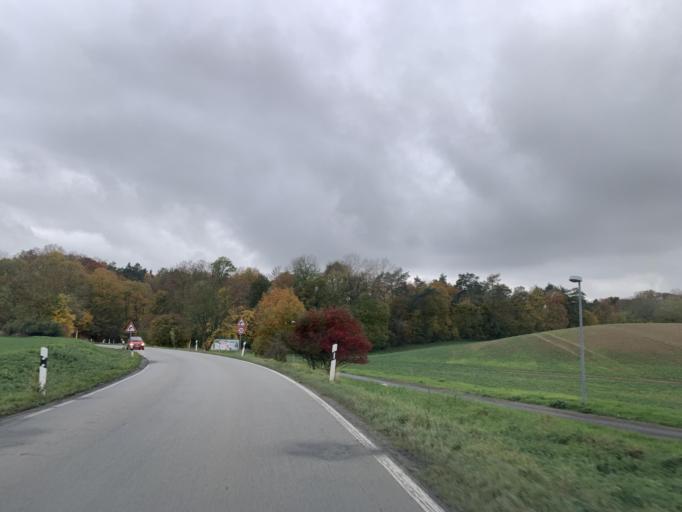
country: DE
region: Mecklenburg-Vorpommern
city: Neverin
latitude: 53.5848
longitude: 13.3285
